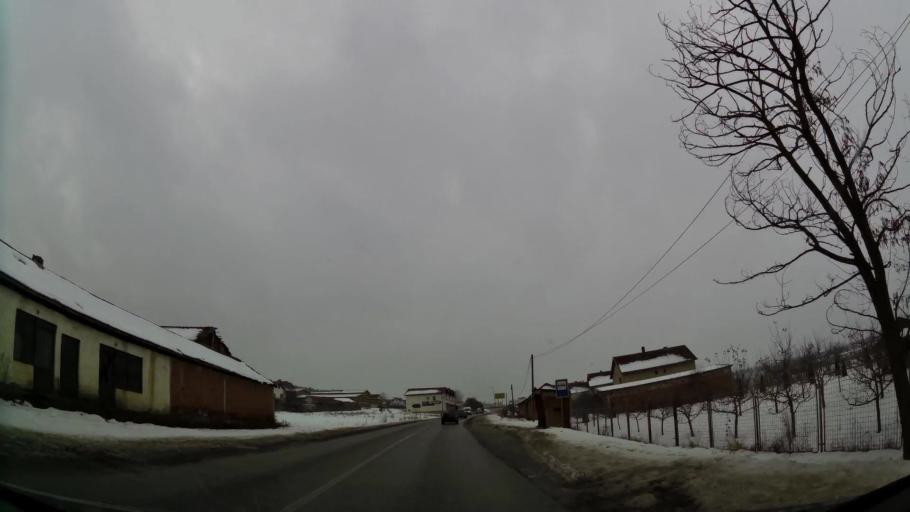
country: XK
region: Pristina
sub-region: Komuna e Prishtines
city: Pristina
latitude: 42.7297
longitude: 21.1434
